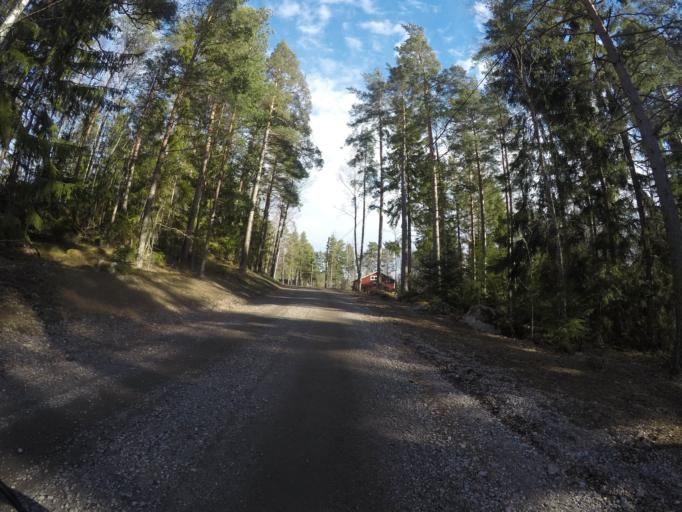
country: SE
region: Vaestmanland
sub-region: Kungsors Kommun
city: Kungsoer
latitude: 59.4348
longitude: 16.1394
